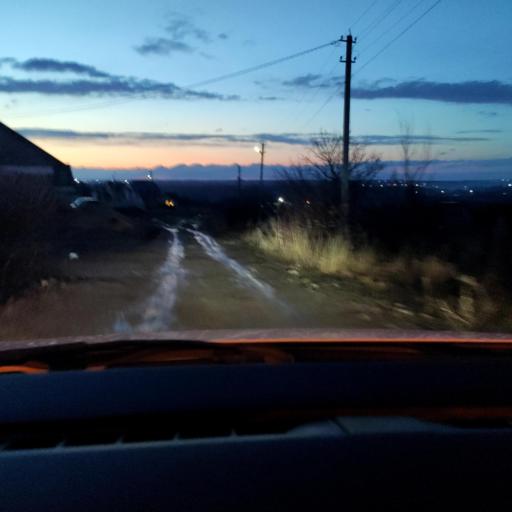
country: RU
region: Voronezj
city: Semiluki
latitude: 51.7142
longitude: 39.0213
